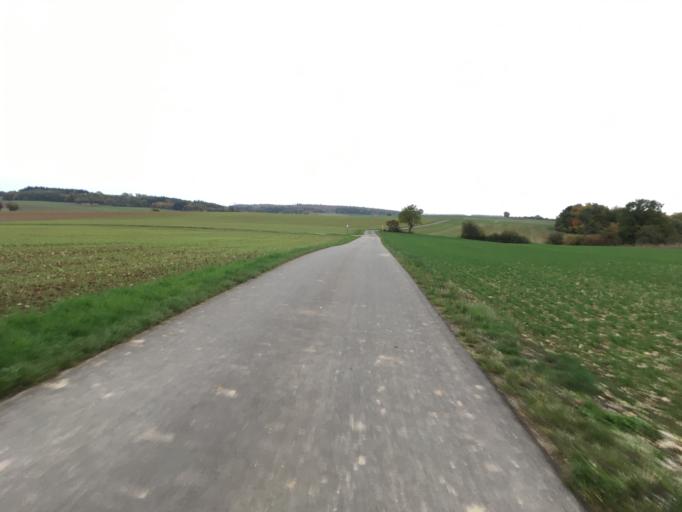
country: DE
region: Baden-Wuerttemberg
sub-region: Karlsruhe Region
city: Seckach
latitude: 49.4680
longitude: 9.3759
